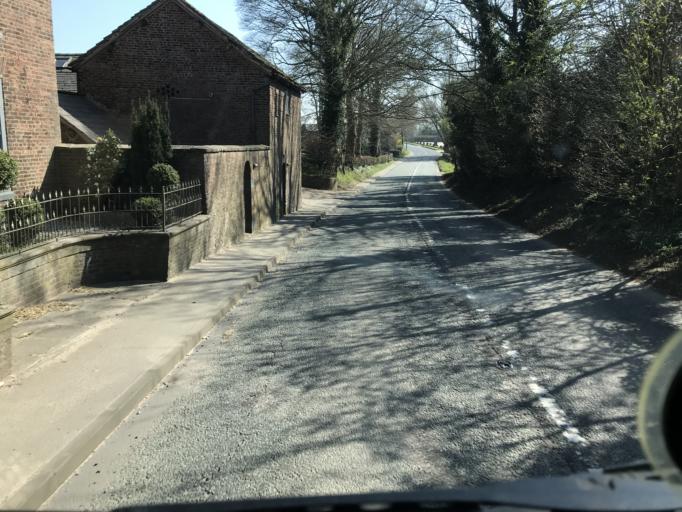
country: GB
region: England
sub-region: Cheshire East
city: Mobberley
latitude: 53.2851
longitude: -2.3313
